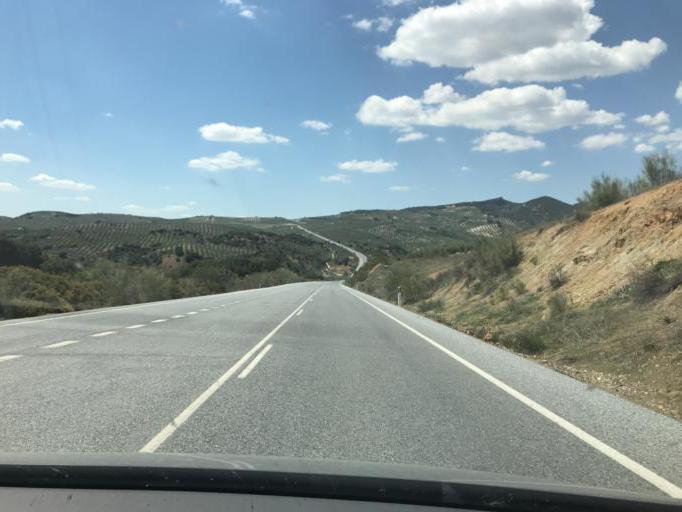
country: ES
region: Andalusia
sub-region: Provincia de Granada
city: Benalua de las Villas
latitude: 37.4261
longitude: -3.7208
